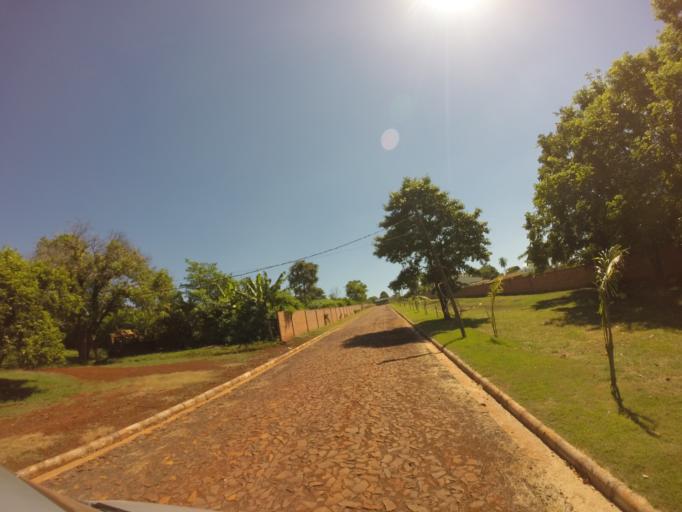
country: PY
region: Alto Parana
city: Ciudad del Este
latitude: -25.4390
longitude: -54.6483
